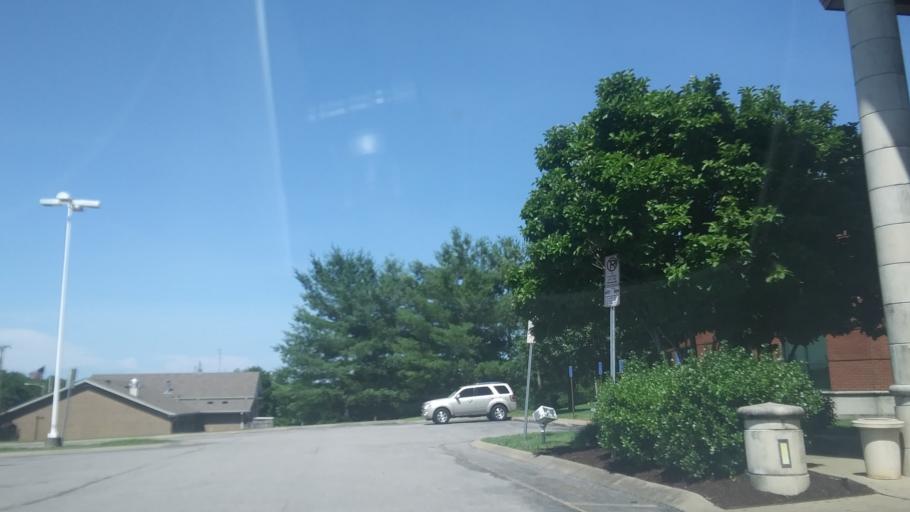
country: US
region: Tennessee
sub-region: Davidson County
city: Oak Hill
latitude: 36.0892
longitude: -86.6878
